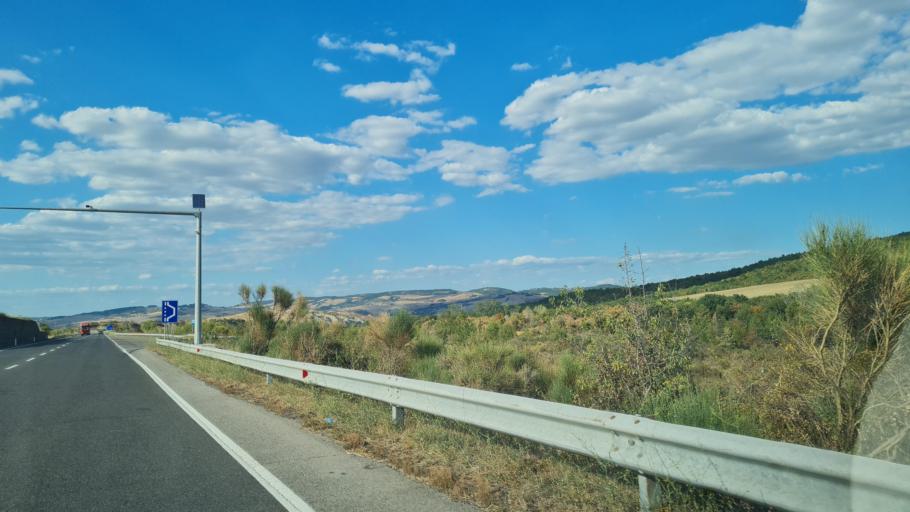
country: IT
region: Tuscany
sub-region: Provincia di Siena
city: Castiglione d'Orcia
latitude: 42.9737
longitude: 11.7061
